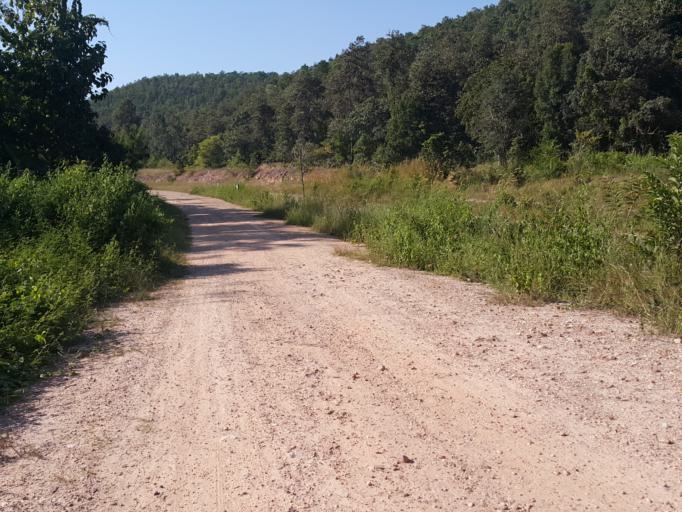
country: TH
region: Chiang Mai
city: Mae On
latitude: 18.7879
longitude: 99.1999
